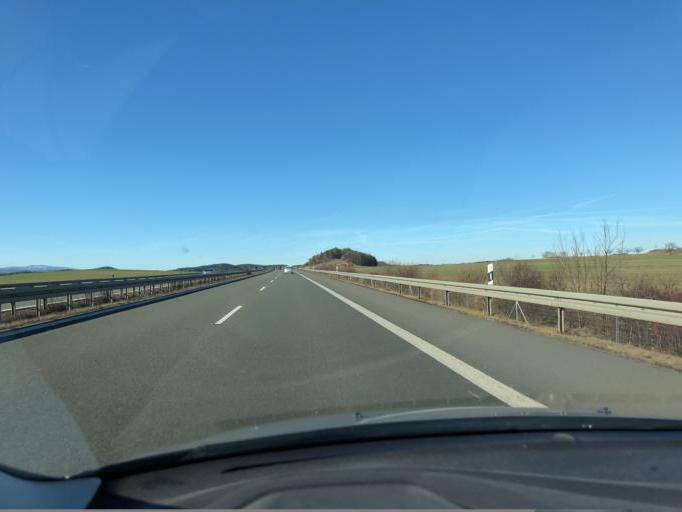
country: DE
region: Saxony-Anhalt
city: Westerhausen
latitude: 51.8150
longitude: 11.0917
